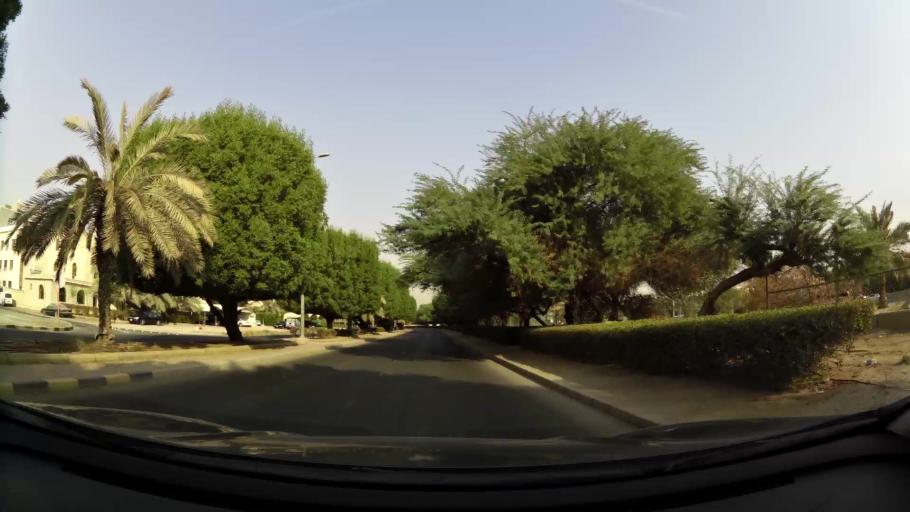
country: KW
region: Muhafazat Hawalli
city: Salwa
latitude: 29.2796
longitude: 48.0777
